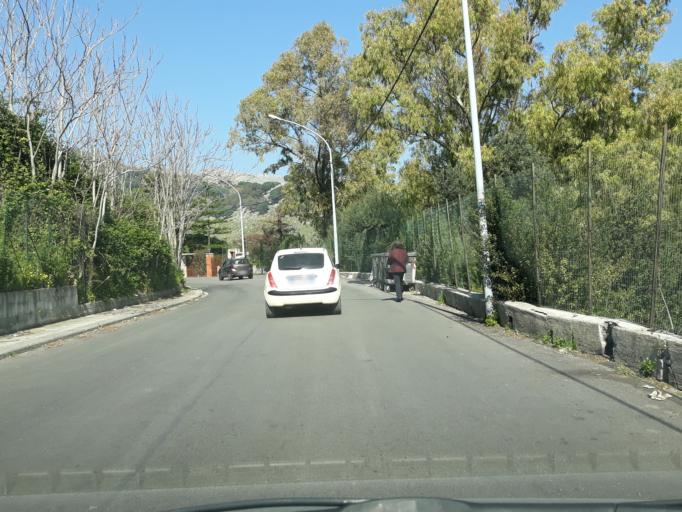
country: IT
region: Sicily
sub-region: Palermo
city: Piano dei Geli
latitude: 38.1149
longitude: 13.2944
